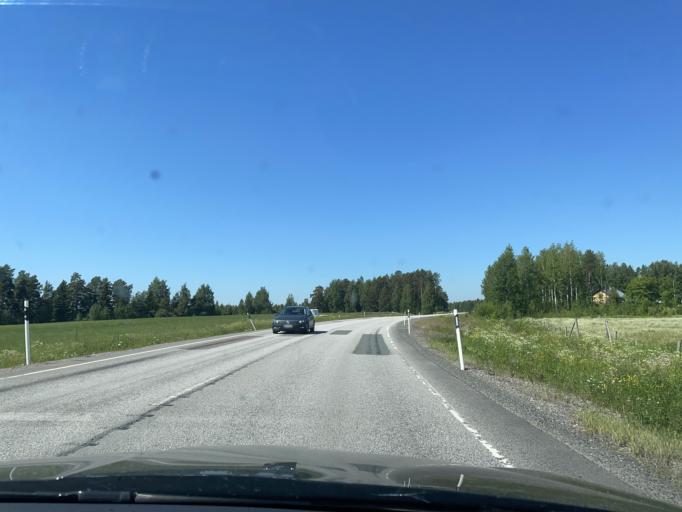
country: FI
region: Central Finland
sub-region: Saarijaervi-Viitasaari
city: Viitasaari
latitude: 63.1410
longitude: 25.8376
